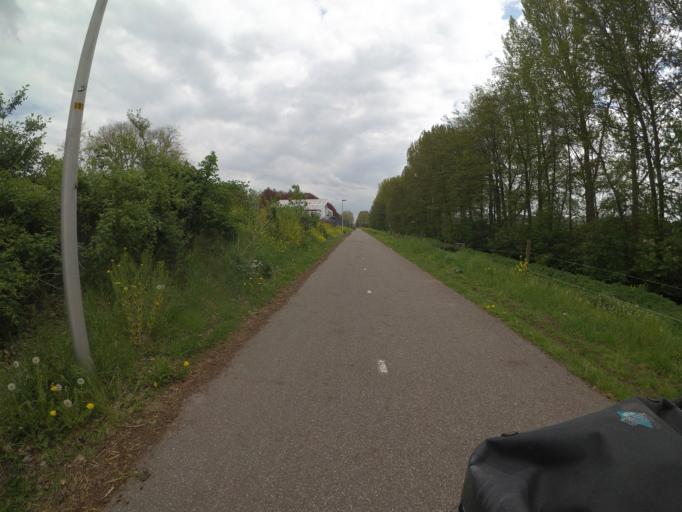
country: NL
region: North Brabant
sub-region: Gemeente Waalwijk
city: Waspik
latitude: 51.6824
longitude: 4.9424
